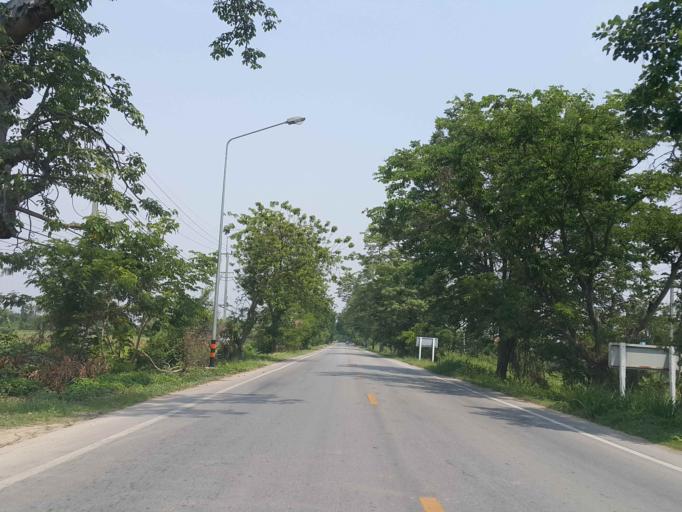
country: TH
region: Chiang Mai
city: Mae Taeng
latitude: 19.0460
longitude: 98.9652
